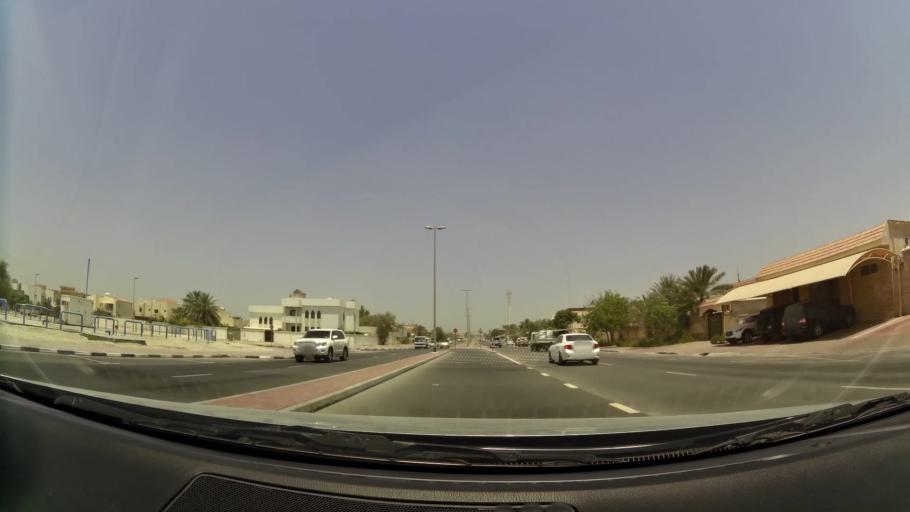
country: AE
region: Dubai
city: Dubai
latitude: 25.1949
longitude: 55.2534
